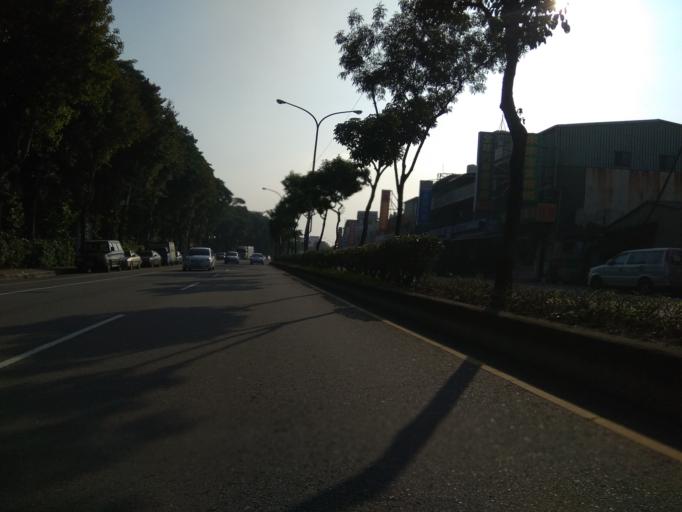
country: TW
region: Taiwan
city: Daxi
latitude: 24.9363
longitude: 121.2010
